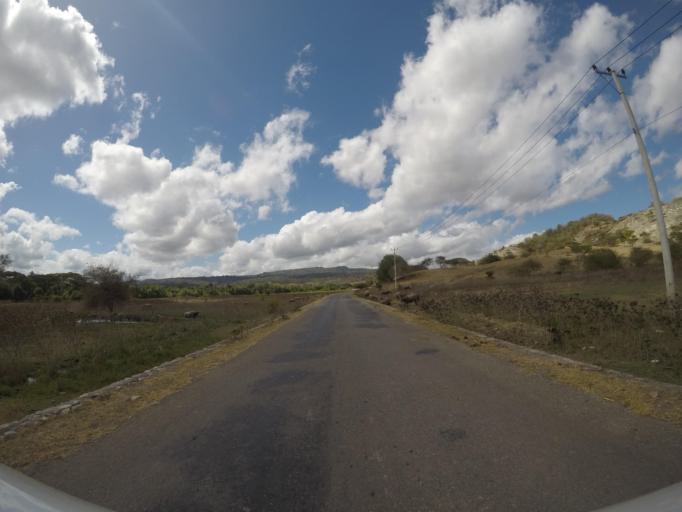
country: TL
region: Lautem
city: Lospalos
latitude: -8.4189
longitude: 126.8282
